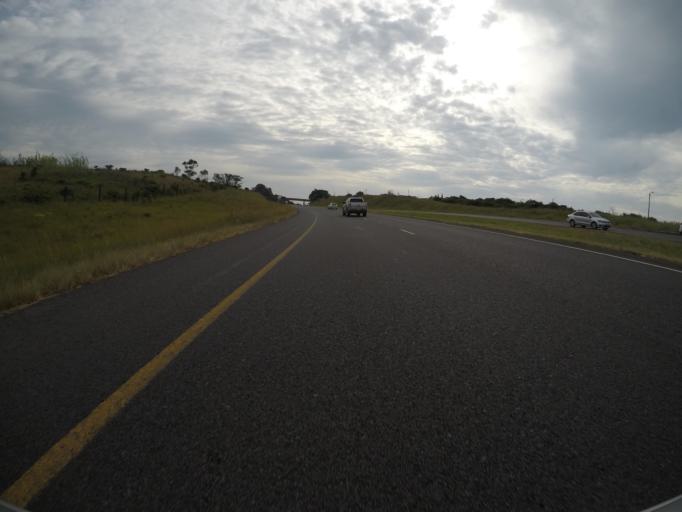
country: ZA
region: Eastern Cape
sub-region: Buffalo City Metropolitan Municipality
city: East London
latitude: -32.9696
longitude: 27.8717
